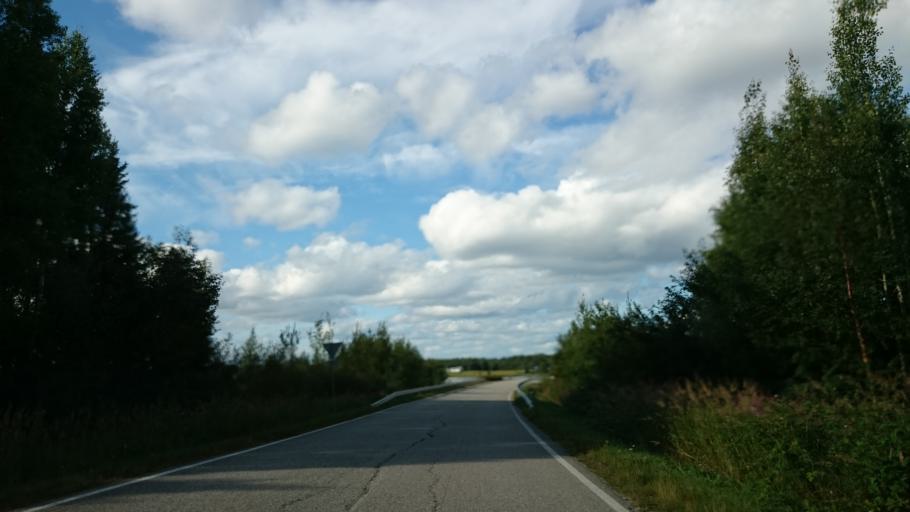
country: FI
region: Kainuu
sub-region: Kehys-Kainuu
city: Suomussalmi
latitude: 64.7377
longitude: 29.4396
